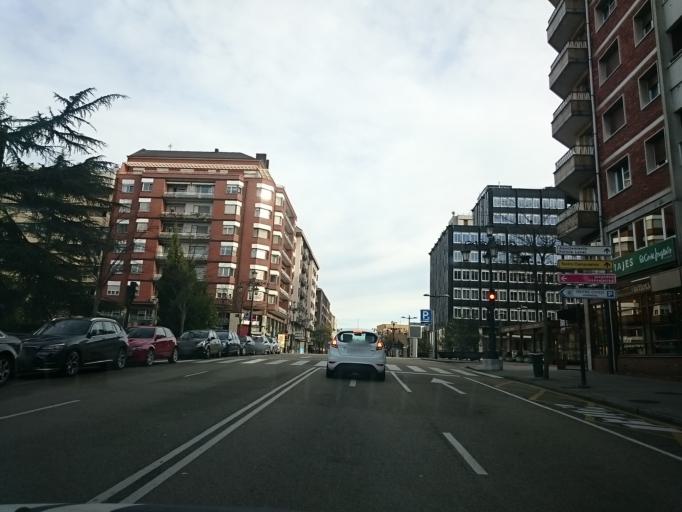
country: ES
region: Asturias
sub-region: Province of Asturias
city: Oviedo
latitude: 43.3616
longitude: -5.8482
